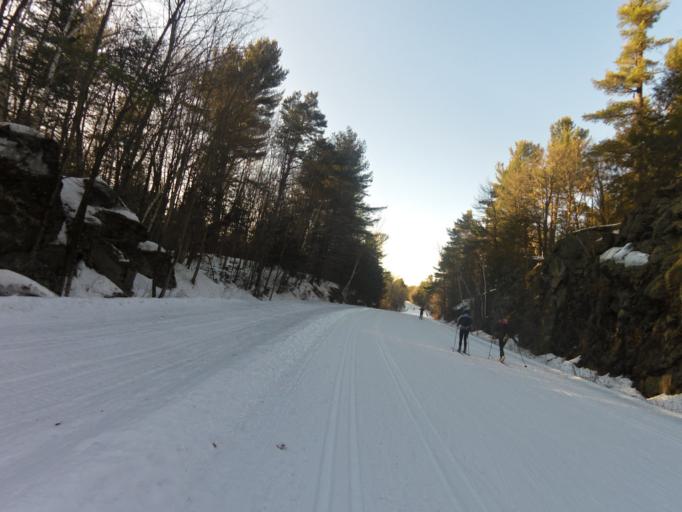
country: CA
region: Quebec
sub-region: Outaouais
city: Gatineau
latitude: 45.5165
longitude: -75.8271
